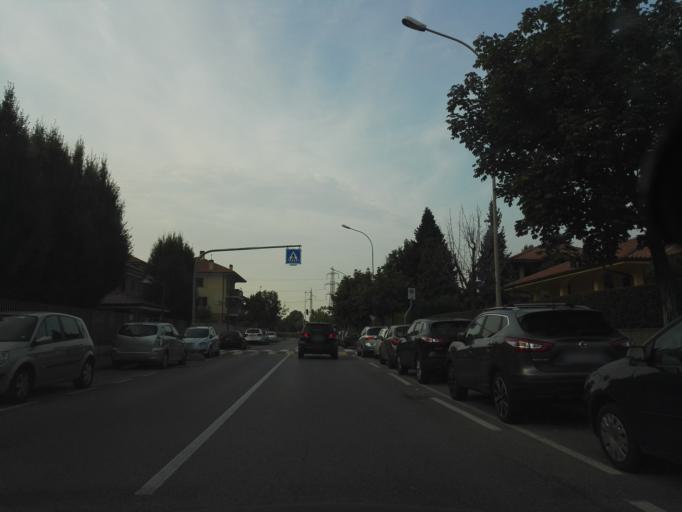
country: IT
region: Lombardy
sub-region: Citta metropolitana di Milano
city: Bettola-Zeloforomagno
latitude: 45.4320
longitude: 9.3069
